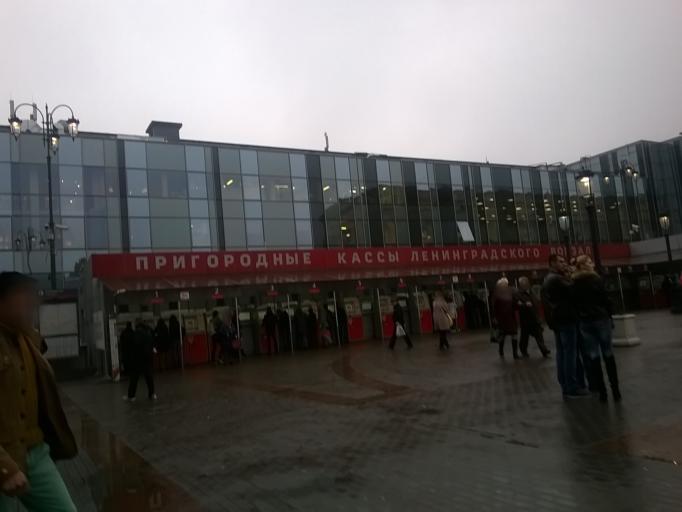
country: RU
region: Moscow
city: Sokol'niki
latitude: 55.7768
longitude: 37.6561
